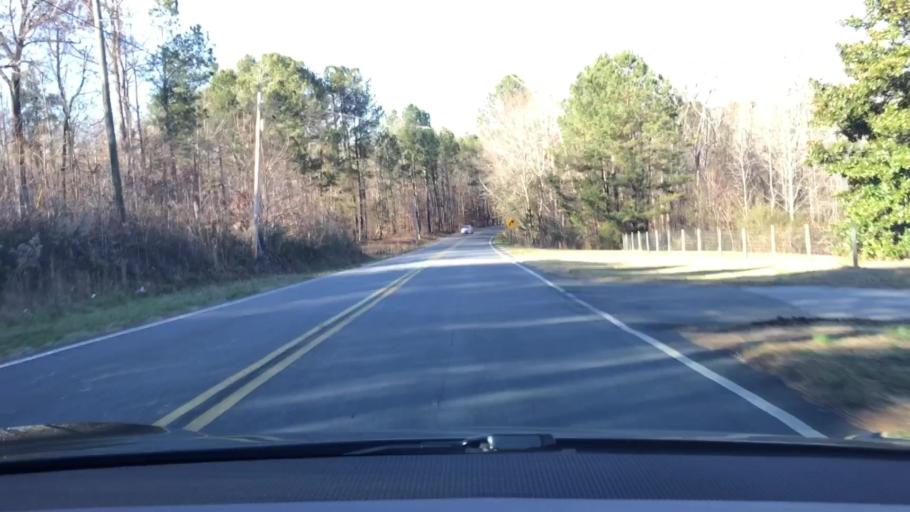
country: US
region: Georgia
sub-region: Barrow County
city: Auburn
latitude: 34.0552
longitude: -83.8511
